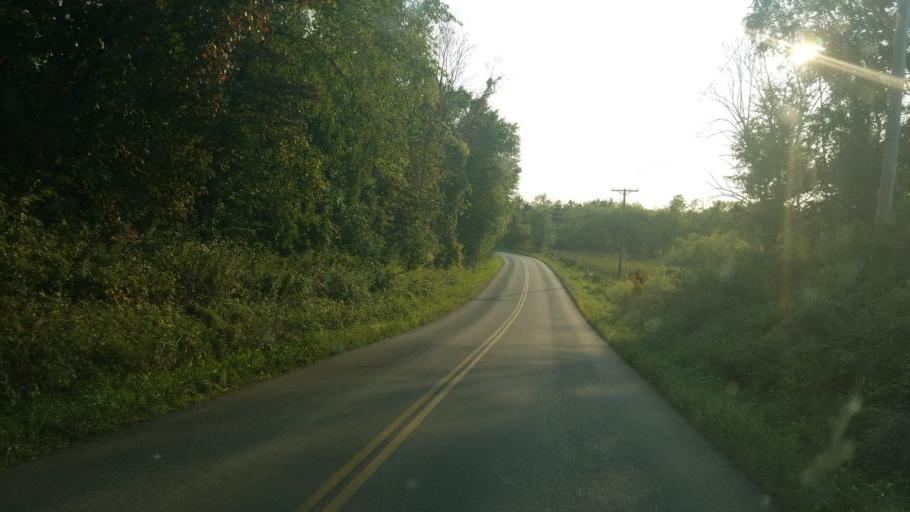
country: US
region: Ohio
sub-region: Wayne County
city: Shreve
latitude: 40.6669
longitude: -81.9499
